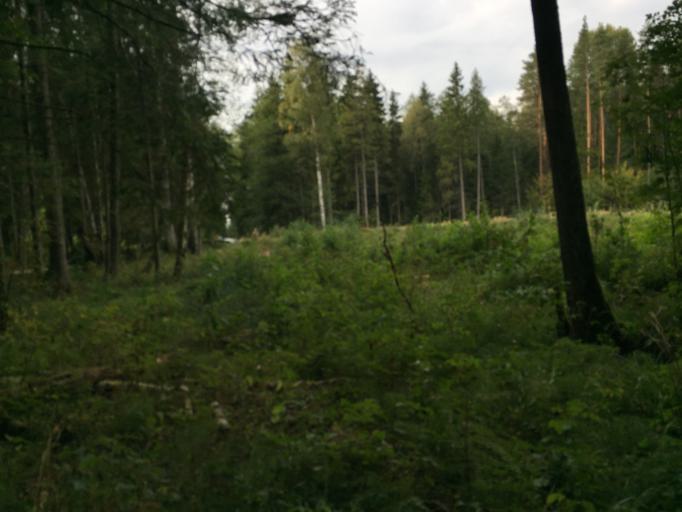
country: LV
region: Ikskile
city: Ikskile
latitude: 56.7573
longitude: 24.4747
